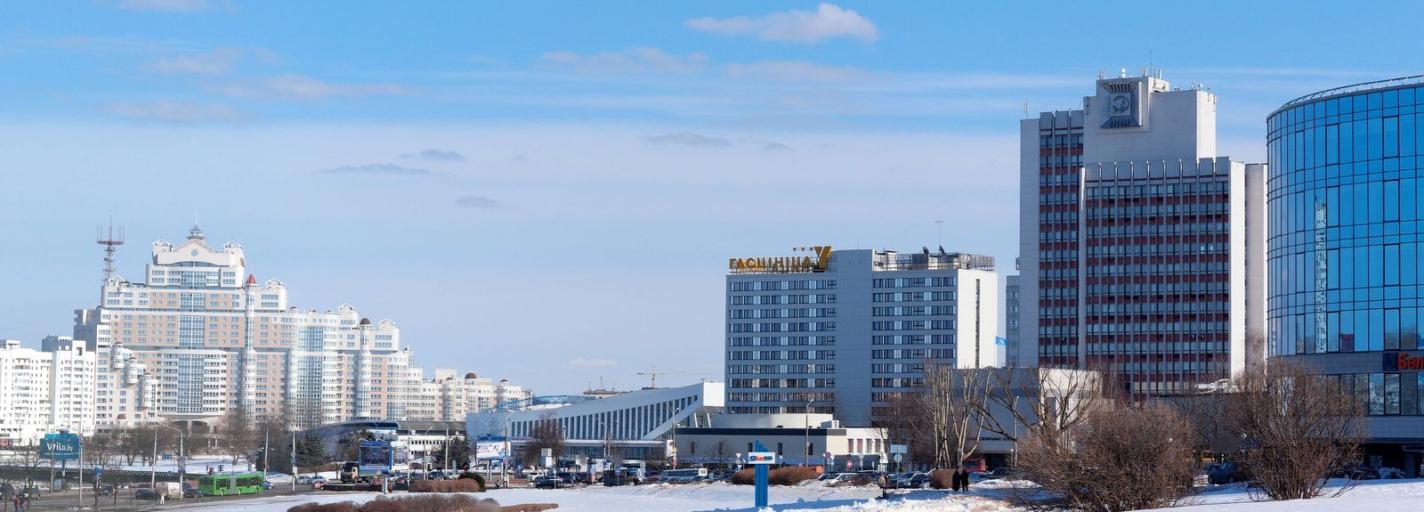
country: BY
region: Minsk
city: Minsk
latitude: 53.9133
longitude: 27.5397
